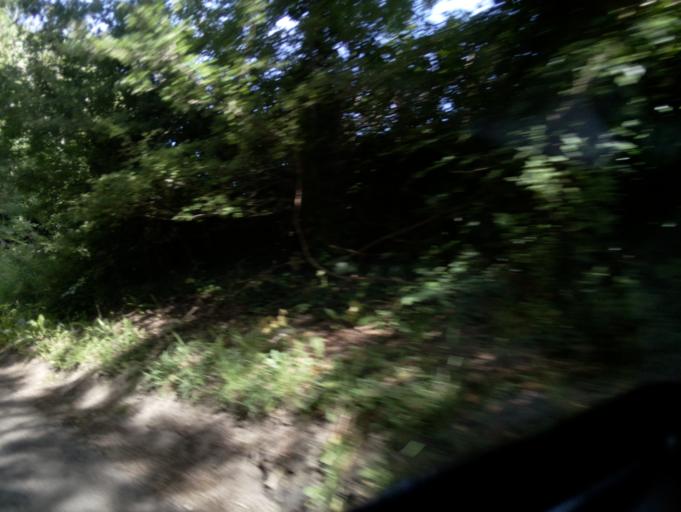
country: GB
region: England
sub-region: Wiltshire
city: Nettleton
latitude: 51.4962
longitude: -2.2518
